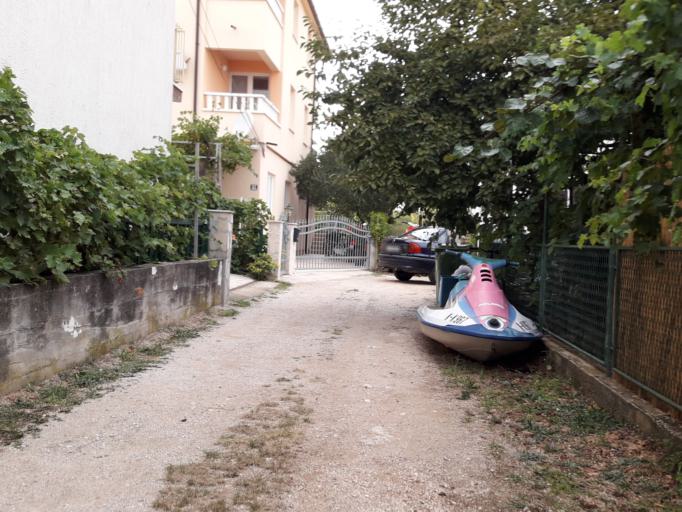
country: HR
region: Sibensko-Kniniska
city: Vodice
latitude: 43.7466
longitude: 15.7990
